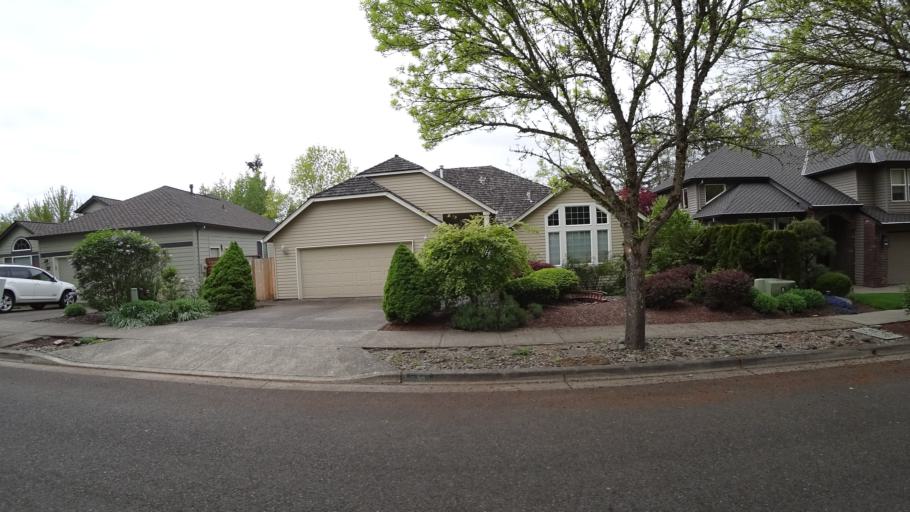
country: US
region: Oregon
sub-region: Washington County
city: Beaverton
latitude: 45.4593
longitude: -122.8335
